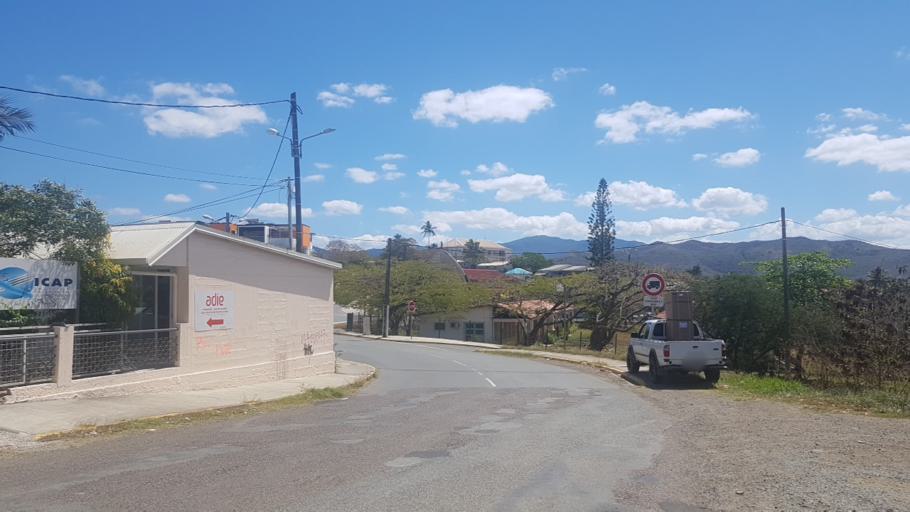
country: NC
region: North Province
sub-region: Kone
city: Kone
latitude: -21.0611
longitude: 164.8626
